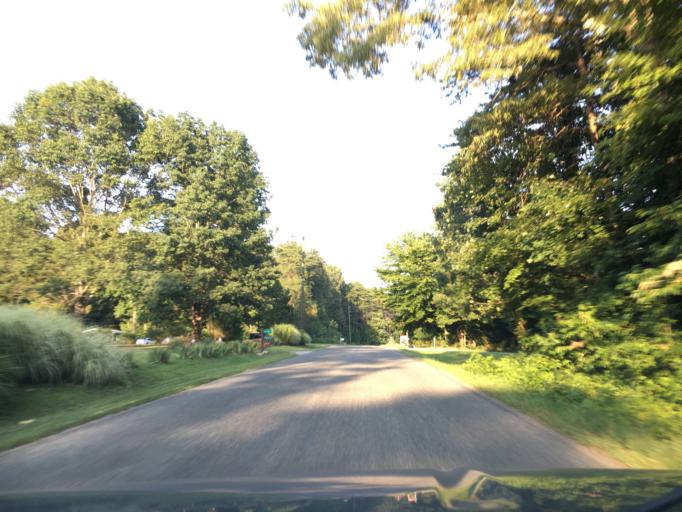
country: US
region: Virginia
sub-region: Pittsylvania County
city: Gretna
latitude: 36.8433
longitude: -79.1833
